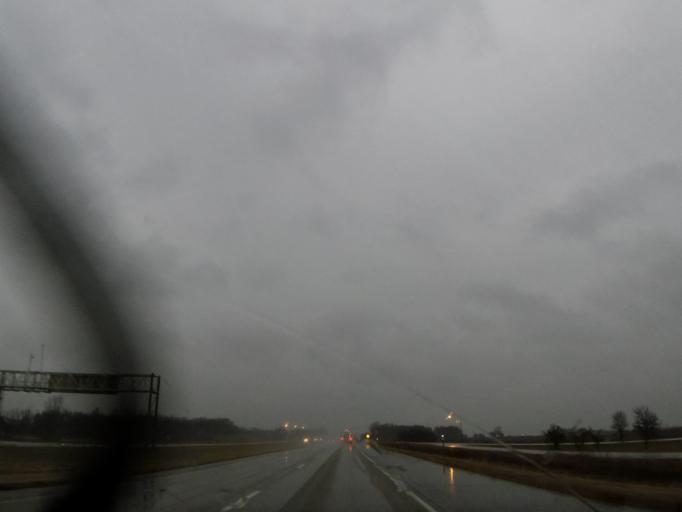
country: US
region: Iowa
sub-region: Cerro Gordo County
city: Clear Lake
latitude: 43.1768
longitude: -93.3560
